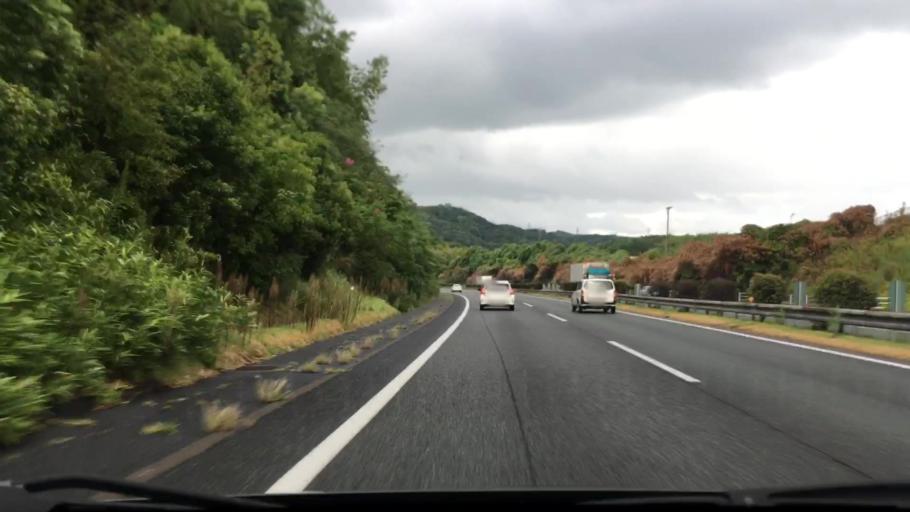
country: JP
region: Fukuoka
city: Miyata
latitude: 33.7442
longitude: 130.6232
